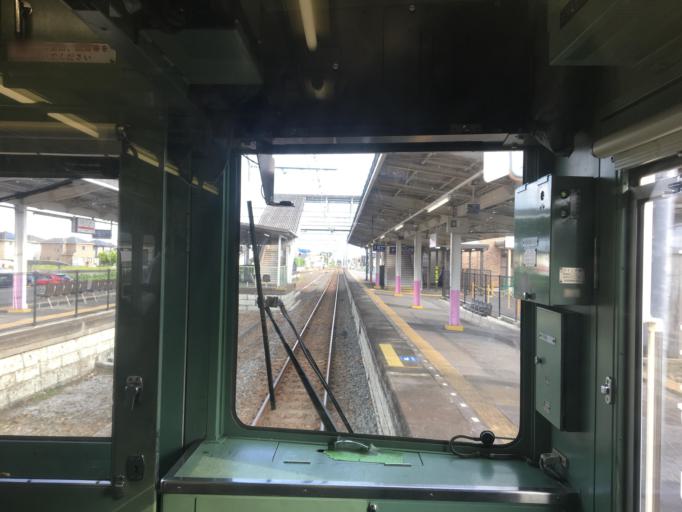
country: JP
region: Tochigi
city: Ashikaga
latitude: 36.3057
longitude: 139.4585
